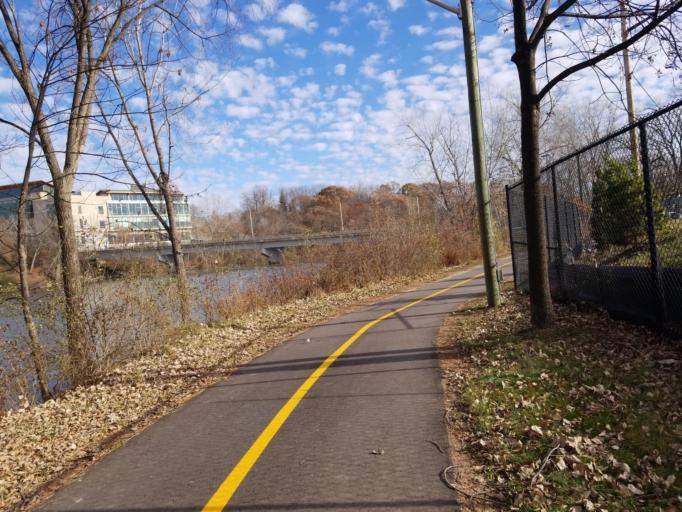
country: US
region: Wisconsin
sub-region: Outagamie County
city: Appleton
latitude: 44.2585
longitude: -88.3987
